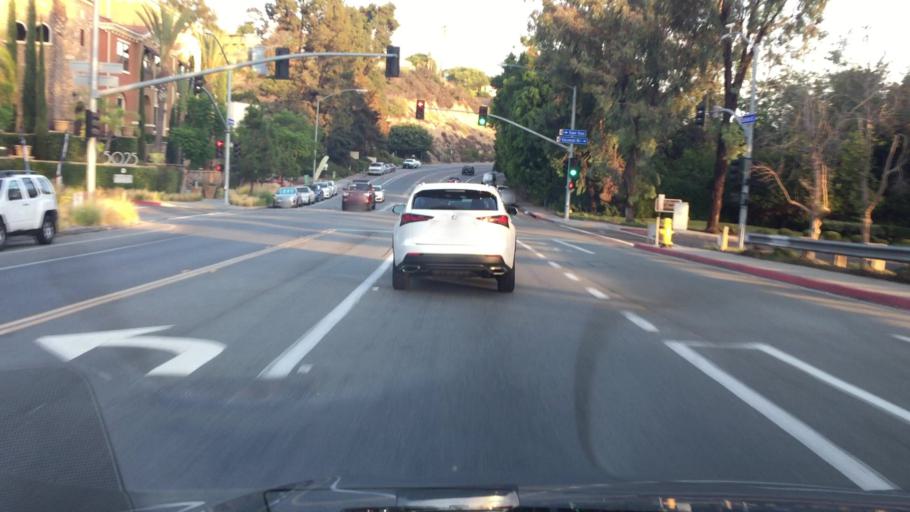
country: US
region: California
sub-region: San Diego County
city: Lemon Grove
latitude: 32.7684
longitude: -117.0852
